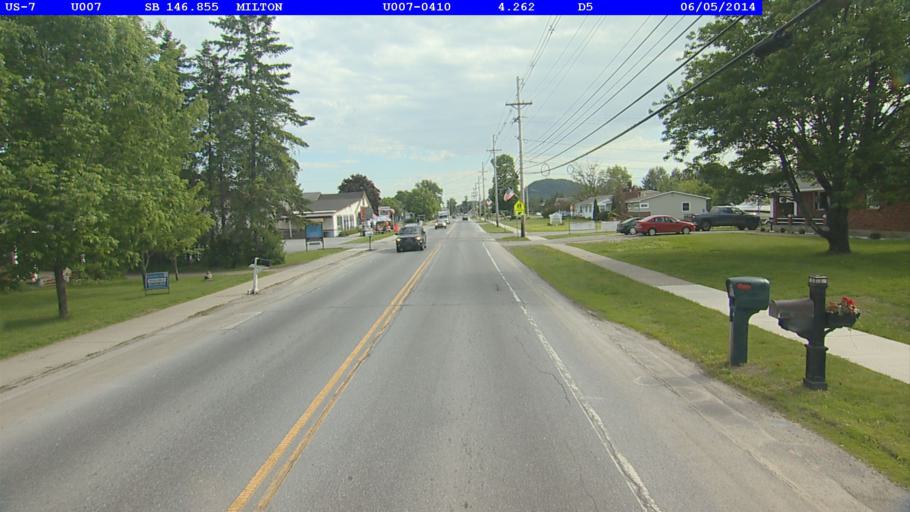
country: US
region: Vermont
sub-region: Chittenden County
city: Milton
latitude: 44.6289
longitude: -73.1164
